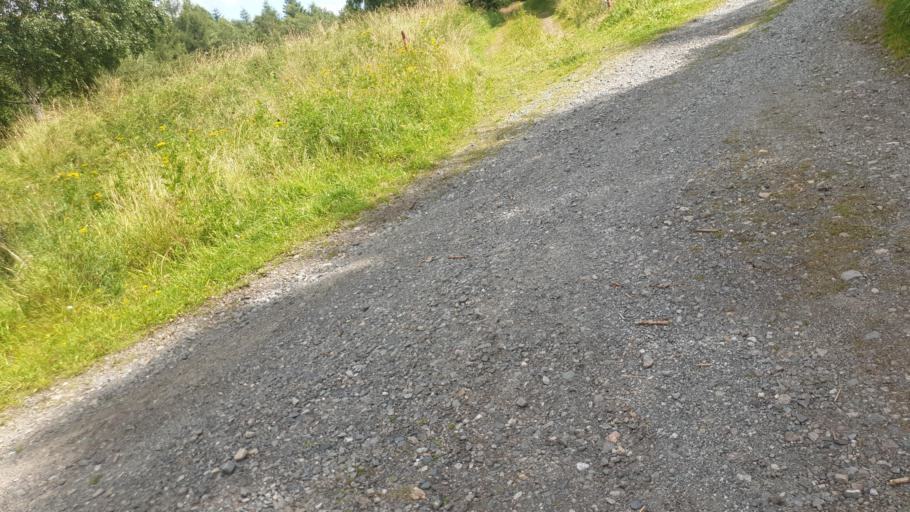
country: CZ
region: Ustecky
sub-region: Okres Chomutov
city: Kovarska
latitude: 50.4303
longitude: 13.0396
